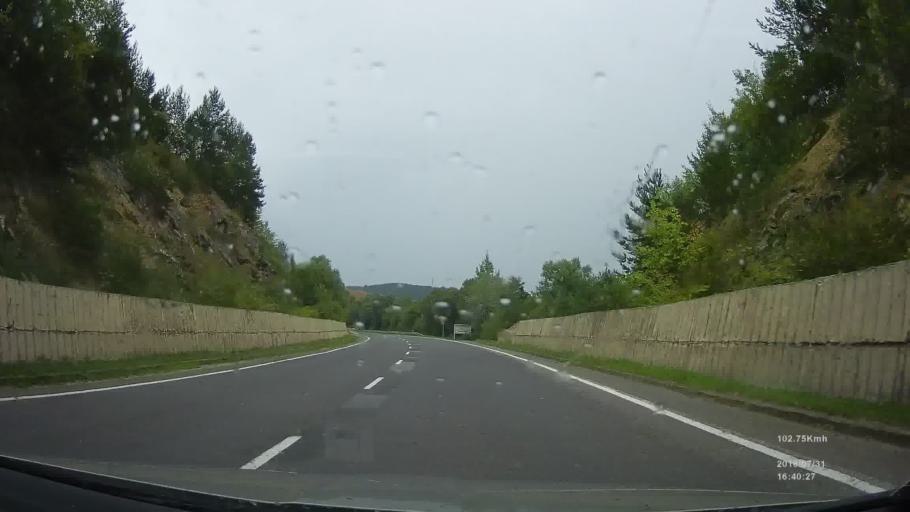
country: SK
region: Presovsky
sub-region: Okres Presov
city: Presov
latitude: 49.1158
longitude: 21.3126
